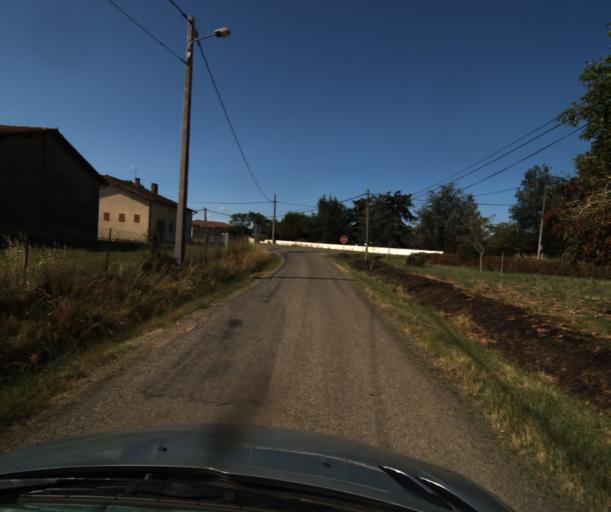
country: FR
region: Midi-Pyrenees
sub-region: Departement du Tarn-et-Garonne
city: Finhan
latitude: 43.9184
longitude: 1.2698
